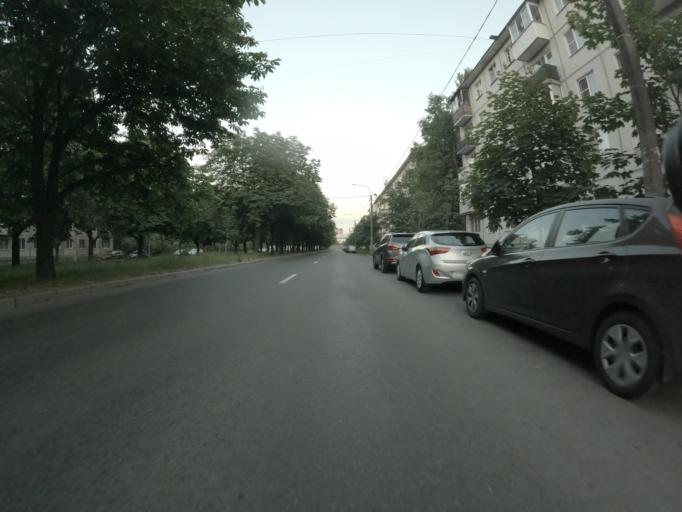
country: RU
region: St.-Petersburg
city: Centralniy
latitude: 59.9235
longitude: 30.4253
